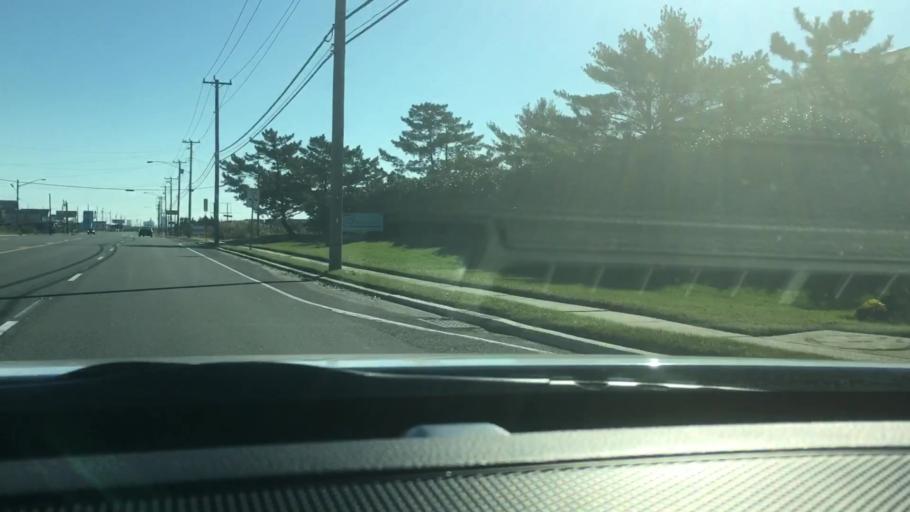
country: US
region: New Jersey
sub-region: Atlantic County
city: Pleasantville
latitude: 39.3845
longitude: -74.5047
